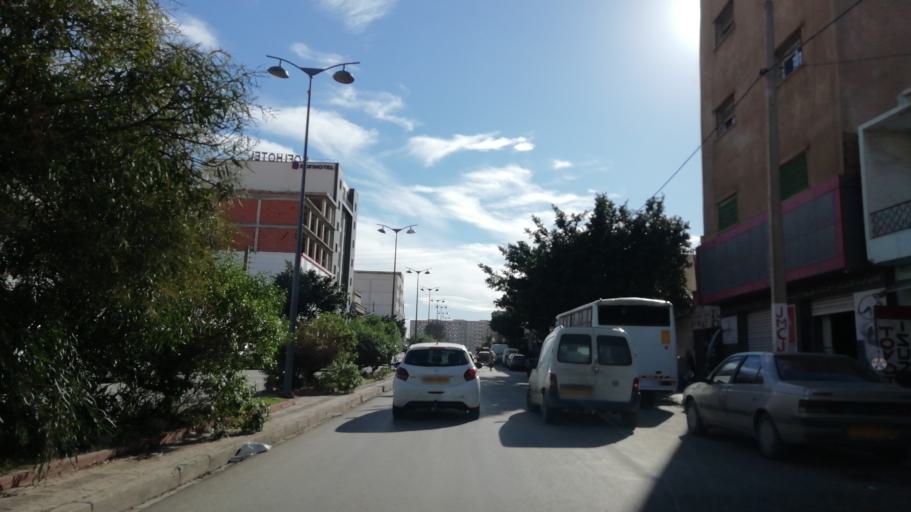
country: DZ
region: Oran
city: Oran
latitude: 35.6938
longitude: -0.6200
